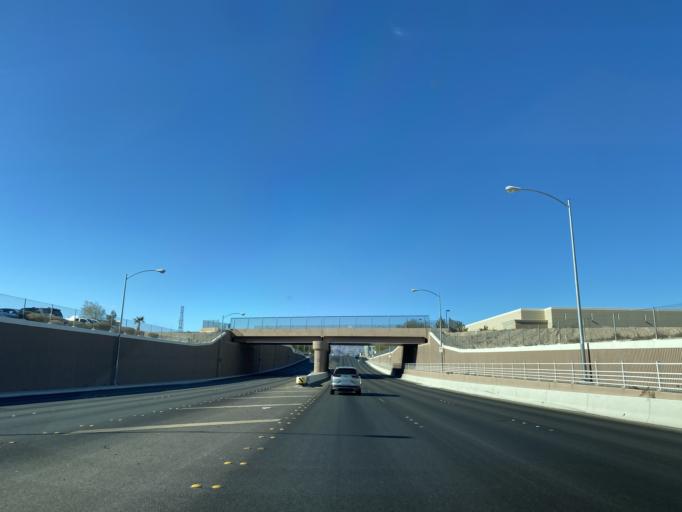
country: US
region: Nevada
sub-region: Clark County
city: Spring Valley
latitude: 36.0718
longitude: -115.2004
